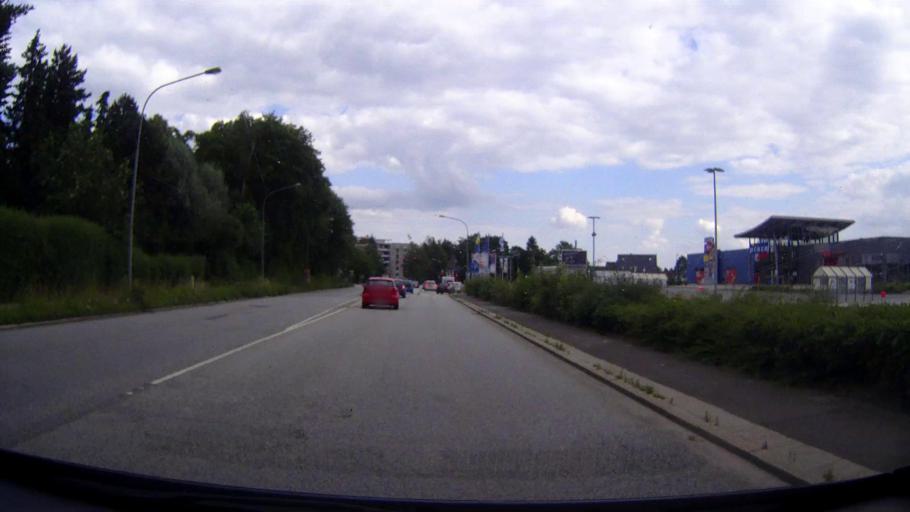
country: DE
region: Schleswig-Holstein
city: Stockelsdorf
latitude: 53.8555
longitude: 10.6367
